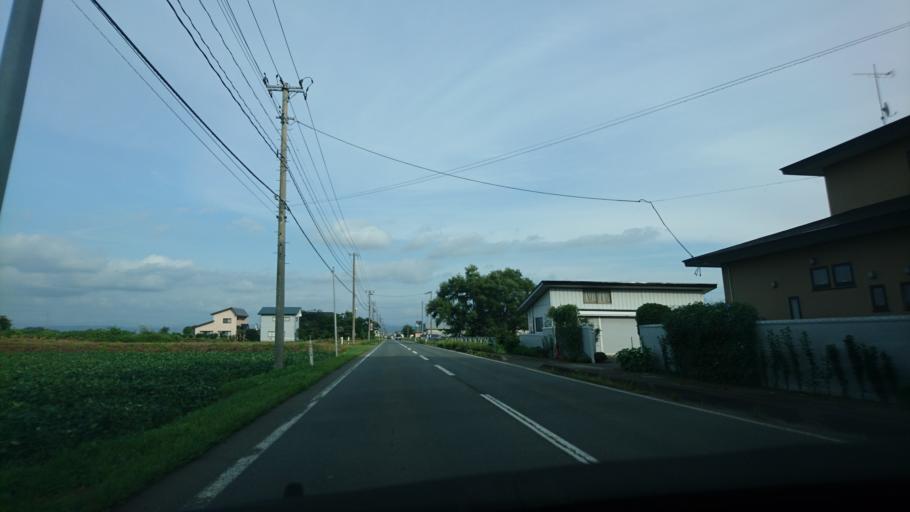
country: JP
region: Iwate
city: Kitakami
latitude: 39.3056
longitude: 141.0079
